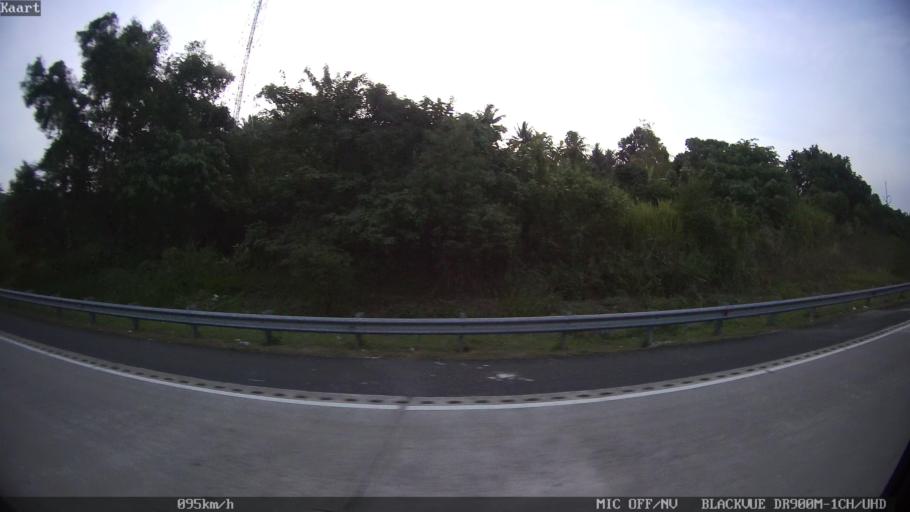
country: ID
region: Lampung
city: Penengahan
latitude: -5.8196
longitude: 105.7365
